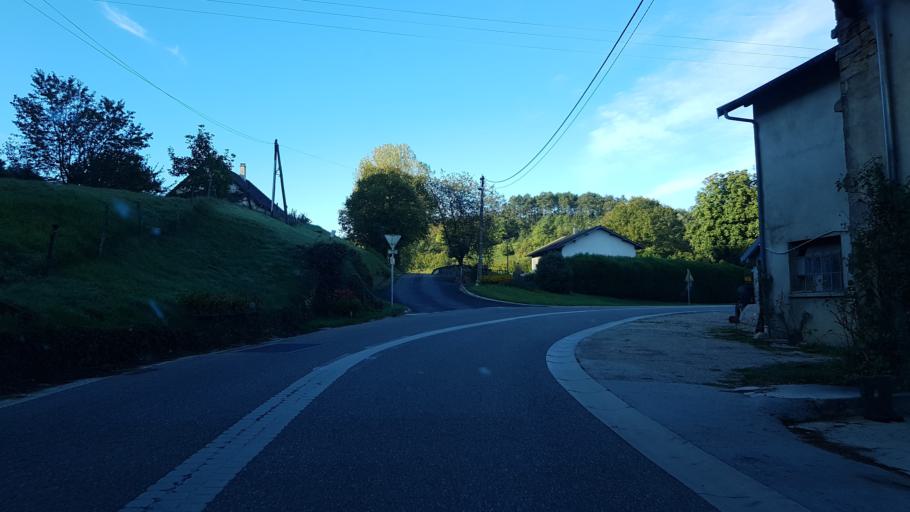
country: FR
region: Franche-Comte
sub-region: Departement du Jura
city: Cousance
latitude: 46.5518
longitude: 5.4921
